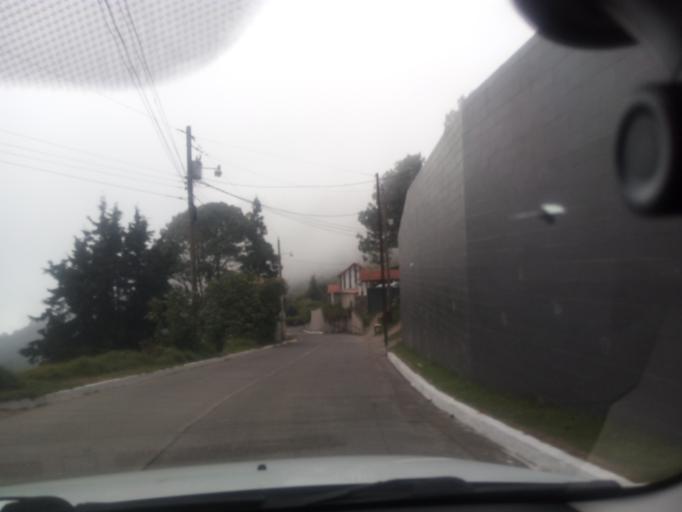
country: GT
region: Sacatepequez
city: San Bartolome Milpas Altas
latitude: 14.5959
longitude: -90.6874
